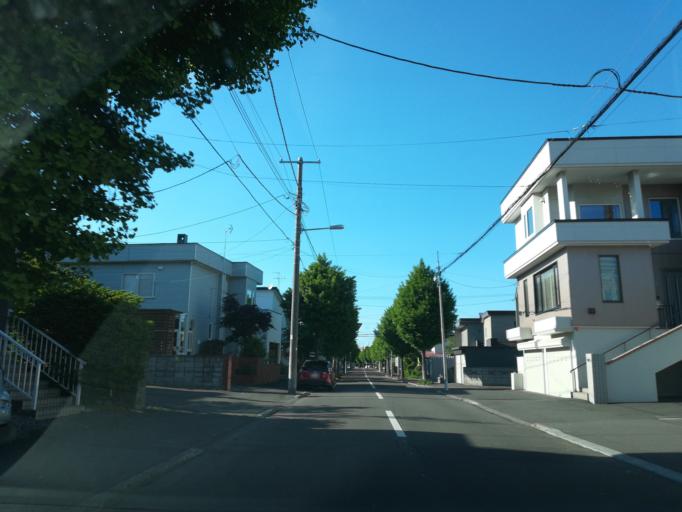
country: JP
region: Hokkaido
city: Sapporo
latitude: 43.0205
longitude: 141.4327
